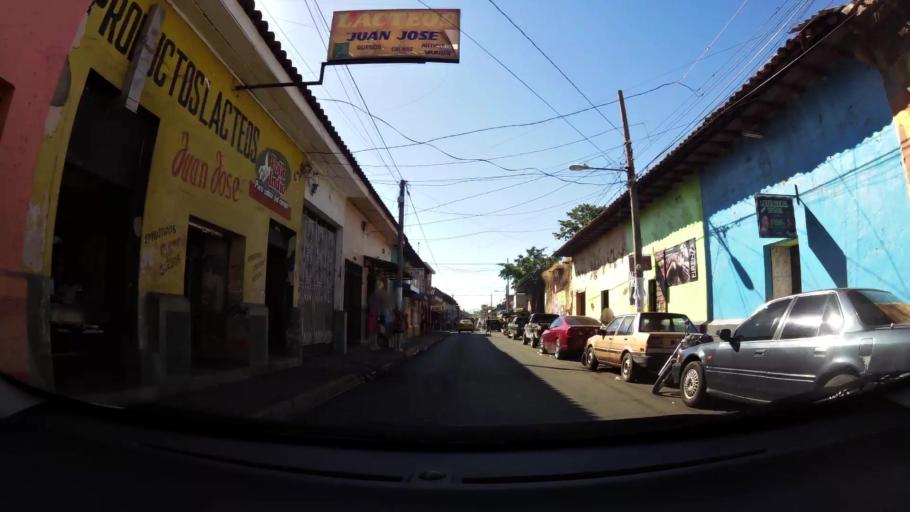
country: SV
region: San Miguel
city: San Miguel
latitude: 13.4812
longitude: -88.1763
